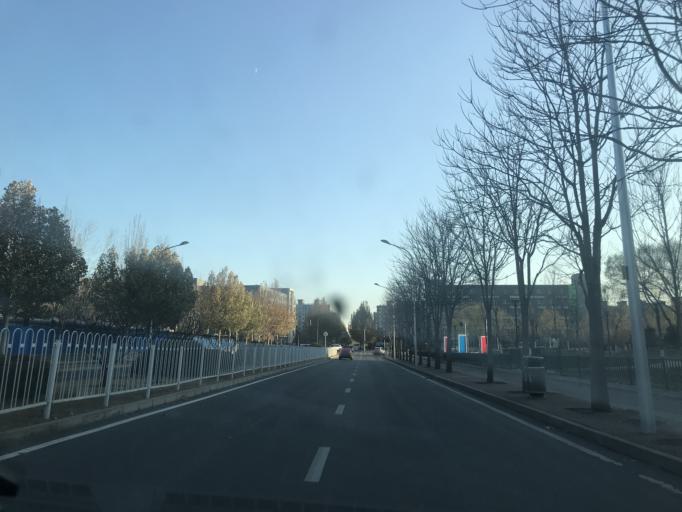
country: CN
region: Beijing
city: Xibeiwang
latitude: 40.0691
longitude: 116.2470
